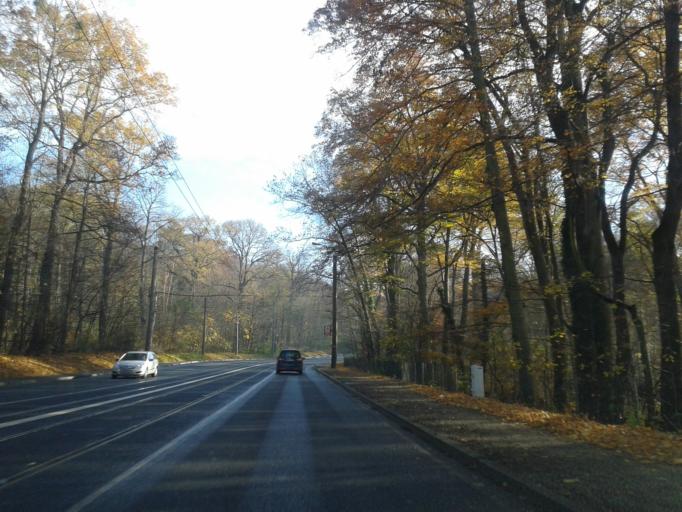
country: DE
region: Saxony
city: Albertstadt
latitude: 51.0656
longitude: 13.8049
